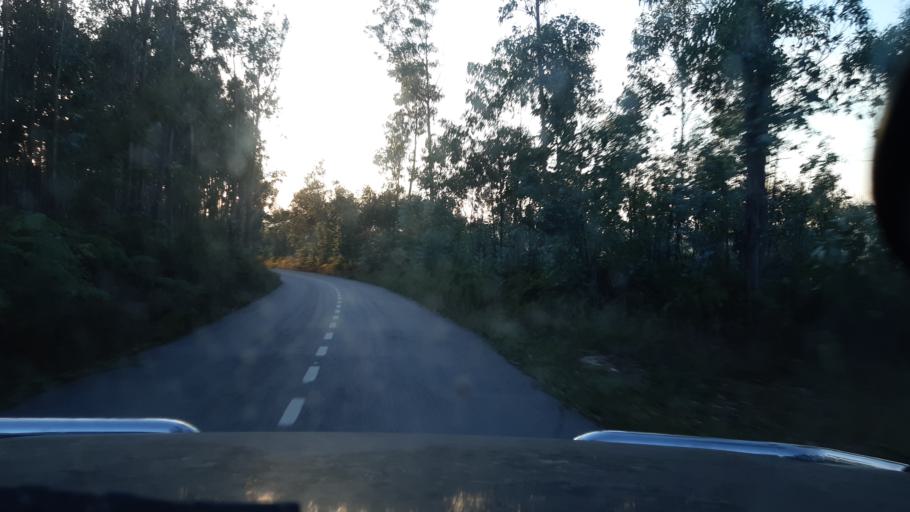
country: PT
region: Aveiro
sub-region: Agueda
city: Aguada de Cima
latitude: 40.5640
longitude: -8.3115
